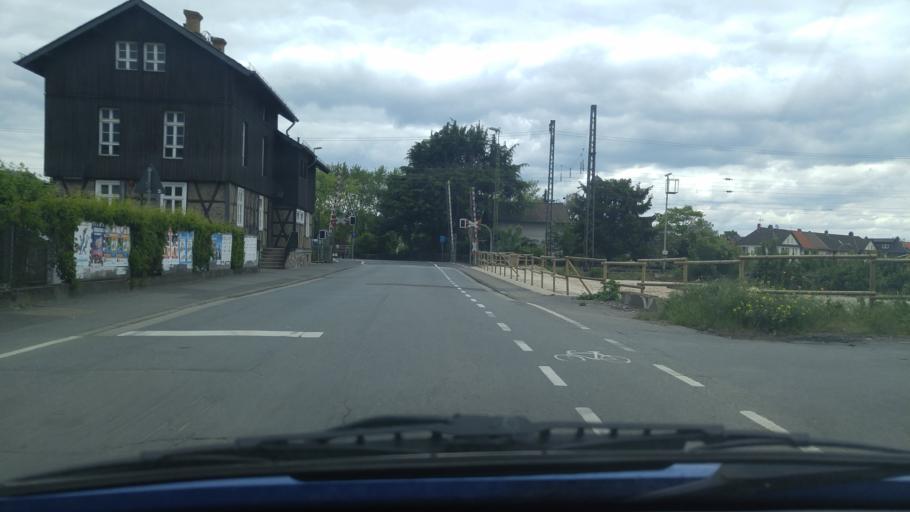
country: DE
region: Hesse
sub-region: Regierungsbezirk Darmstadt
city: Ginsheim-Gustavsburg
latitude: 49.9941
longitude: 8.3206
